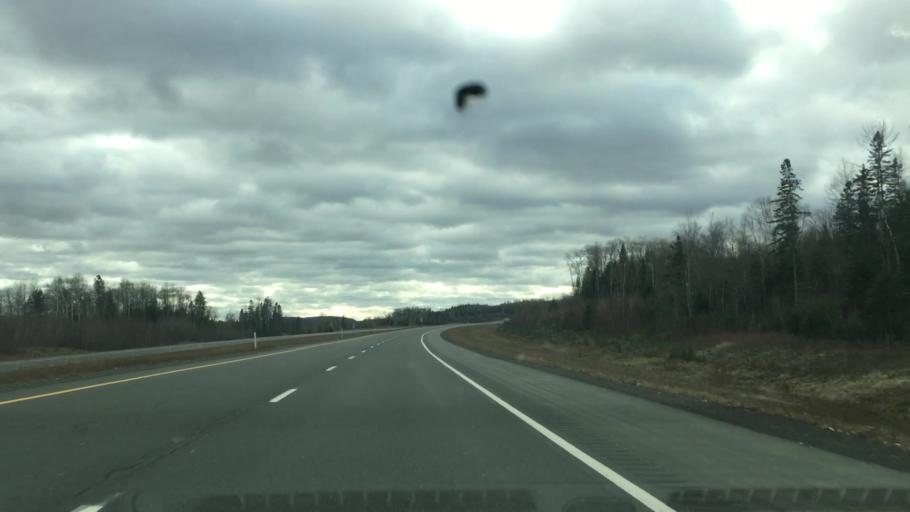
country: US
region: Maine
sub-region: Aroostook County
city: Fort Fairfield
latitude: 46.6745
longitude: -67.7302
